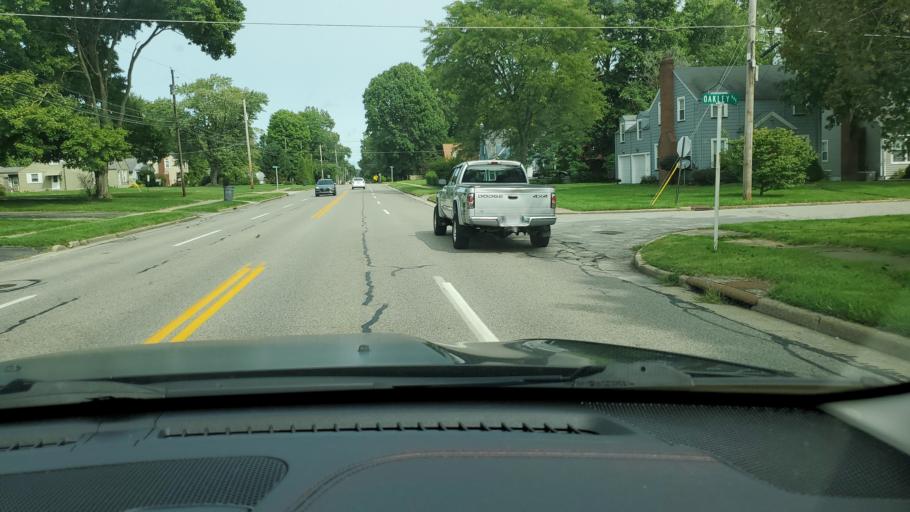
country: US
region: Ohio
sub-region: Mahoning County
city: Boardman
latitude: 41.0314
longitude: -80.6723
